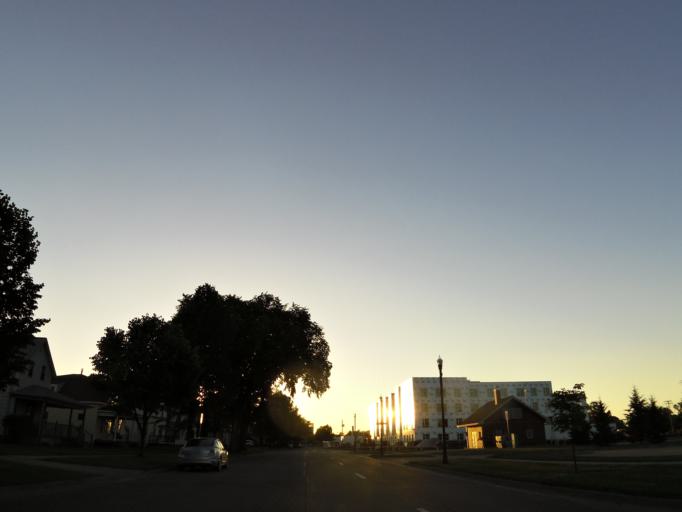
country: US
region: North Dakota
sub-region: Grand Forks County
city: Grand Forks
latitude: 47.9304
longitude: -97.0395
